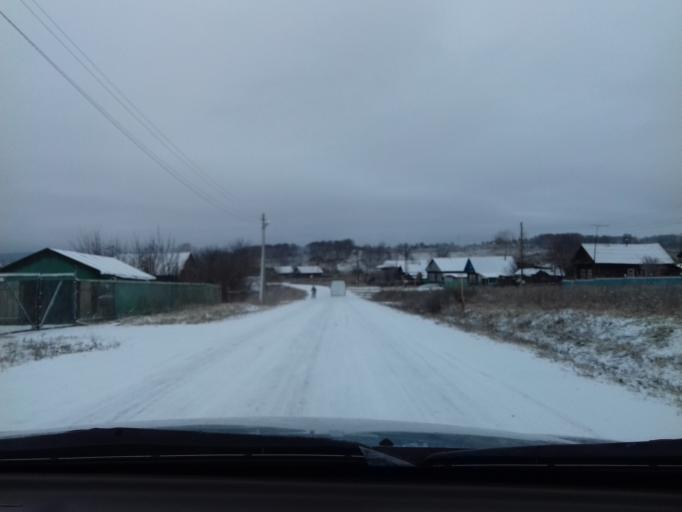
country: RU
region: Sverdlovsk
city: Sarana
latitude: 56.3038
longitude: 57.9798
